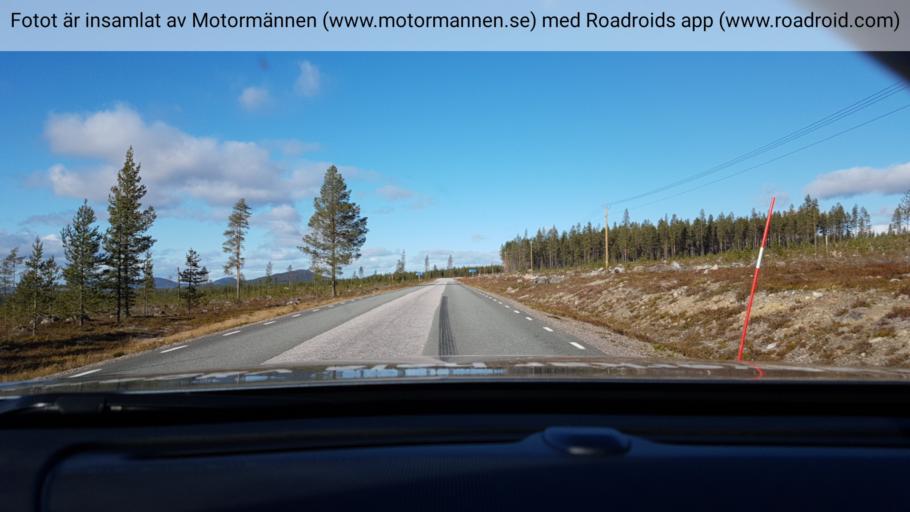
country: SE
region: Vaesterbotten
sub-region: Mala Kommun
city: Mala
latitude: 65.7748
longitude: 18.5208
